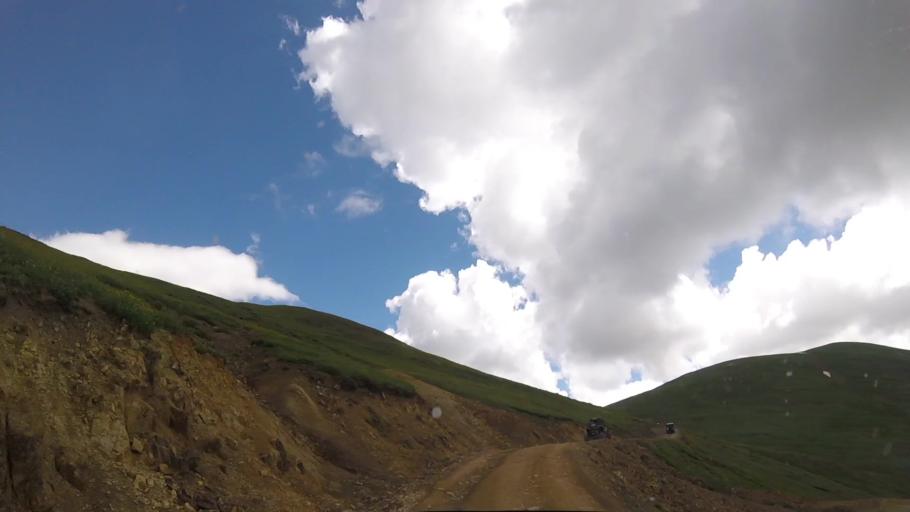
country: US
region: Colorado
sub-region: Ouray County
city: Ouray
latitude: 37.9635
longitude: -107.5761
